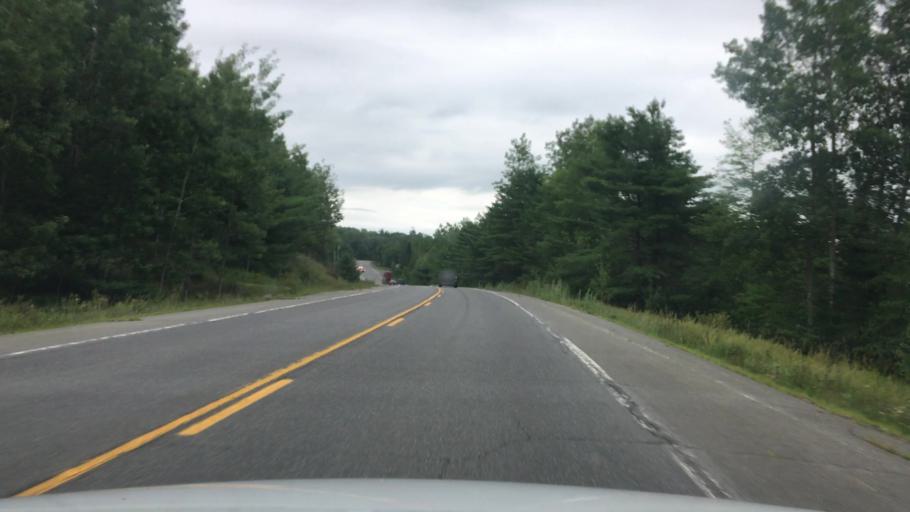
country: US
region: Maine
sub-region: Penobscot County
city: Bradley
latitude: 44.8246
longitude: -68.4000
